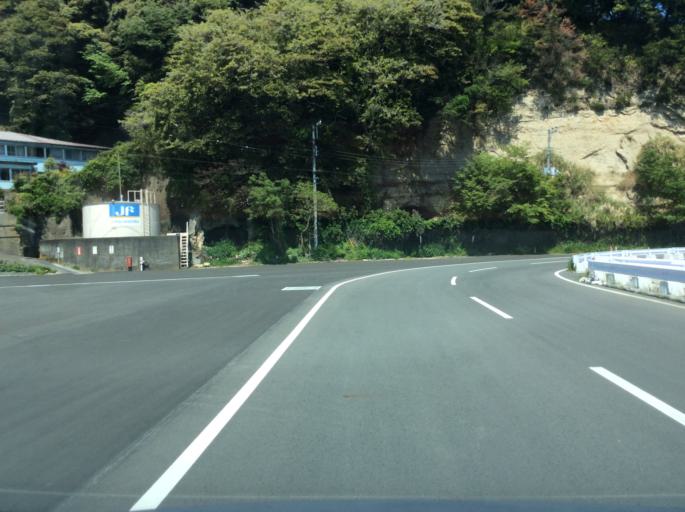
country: JP
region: Ibaraki
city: Kitaibaraki
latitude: 36.8571
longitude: 140.7928
